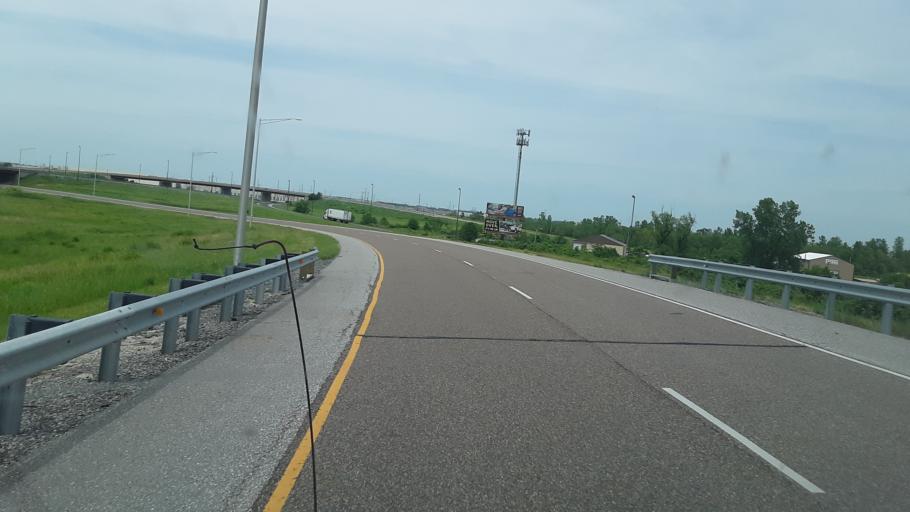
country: US
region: Illinois
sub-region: Madison County
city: Mitchell
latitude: 38.7576
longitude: -90.0406
